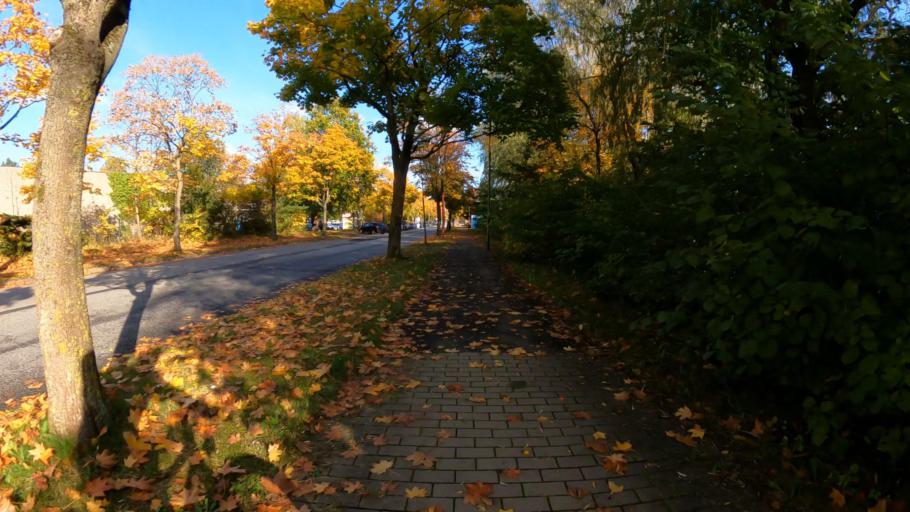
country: DE
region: Schleswig-Holstein
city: Delingsdorf
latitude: 53.6887
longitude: 10.2562
